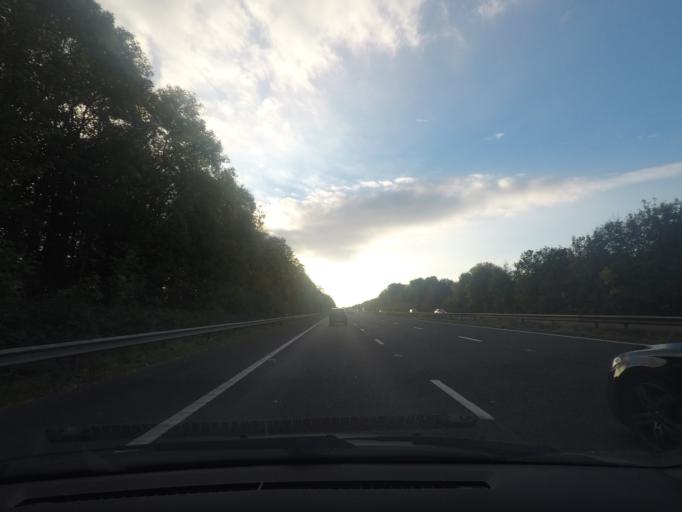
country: GB
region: England
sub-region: North Lincolnshire
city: Scawby
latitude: 53.5497
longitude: -0.5249
